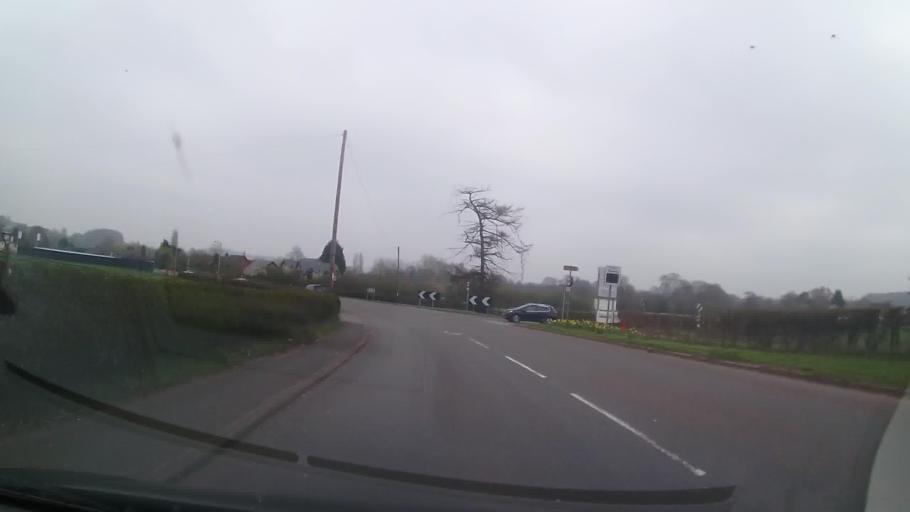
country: GB
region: England
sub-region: Staffordshire
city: Standon
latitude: 52.9561
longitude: -2.3125
